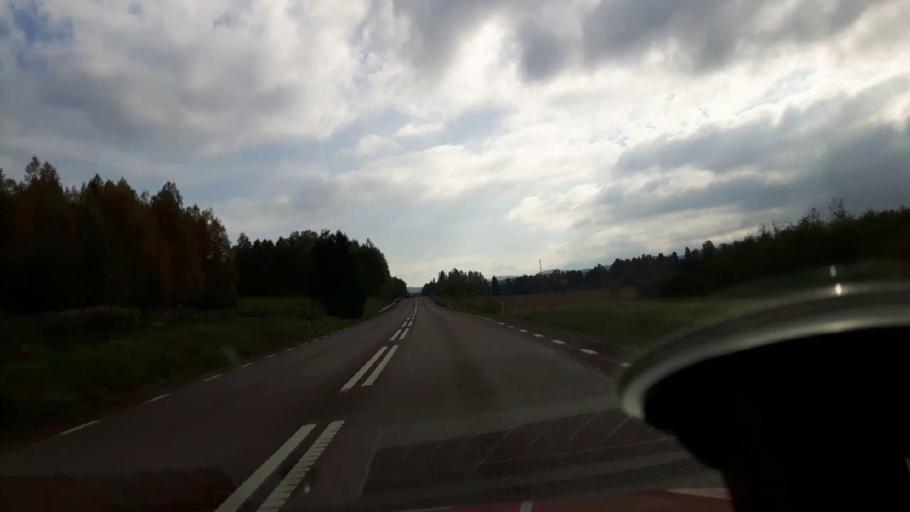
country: SE
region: Gaevleborg
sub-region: Bollnas Kommun
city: Kilafors
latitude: 61.2377
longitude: 16.5524
